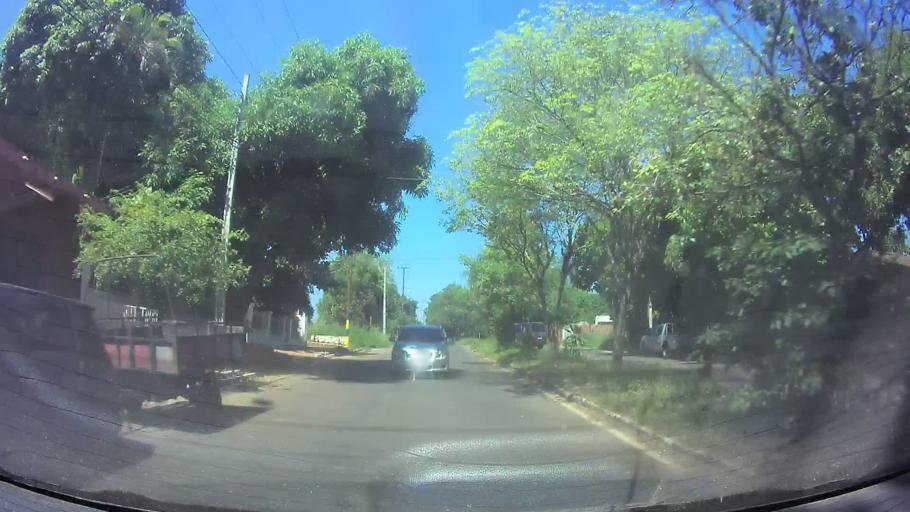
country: PY
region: Central
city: Fernando de la Mora
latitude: -25.2864
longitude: -57.5199
